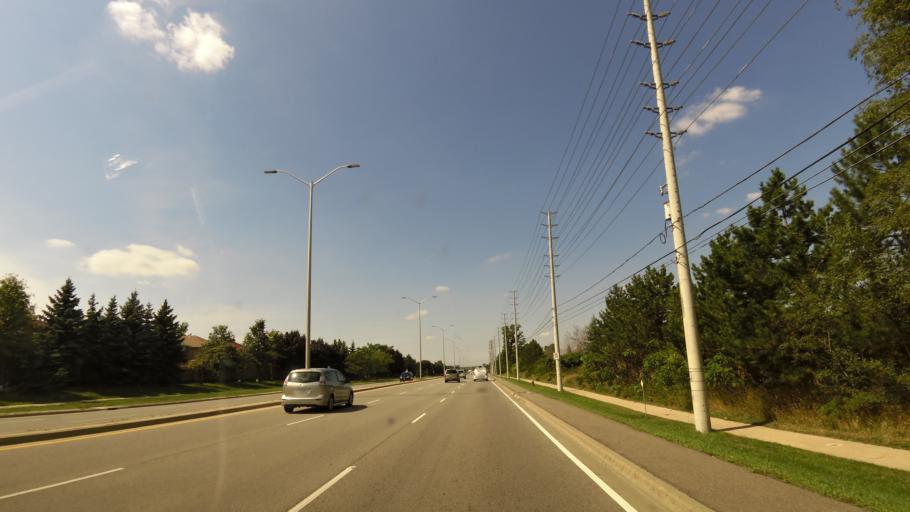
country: CA
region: Ontario
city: Mississauga
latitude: 43.5331
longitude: -79.6607
